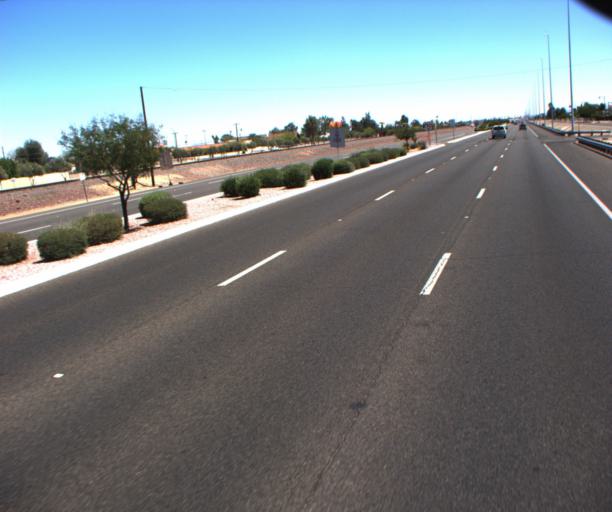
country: US
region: Arizona
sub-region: Maricopa County
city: Surprise
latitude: 33.6284
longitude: -112.3371
